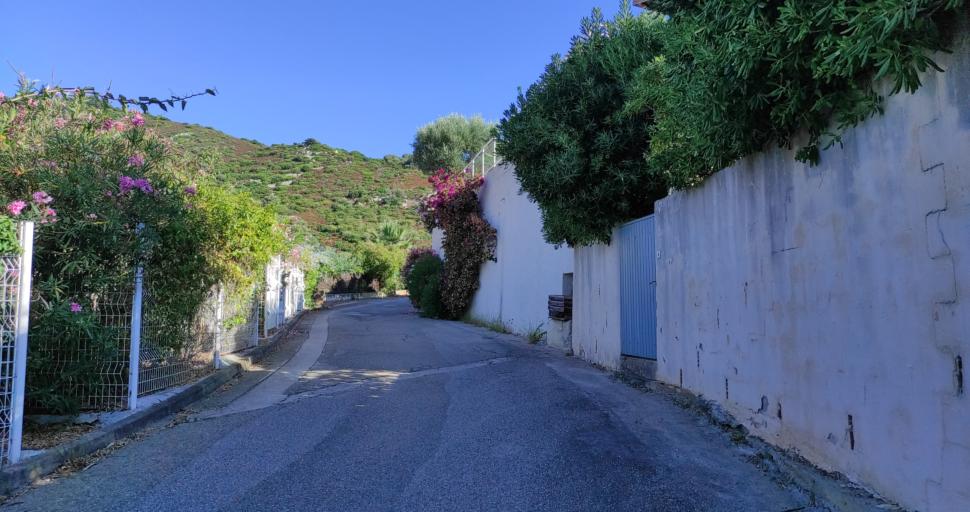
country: FR
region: Corsica
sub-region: Departement de la Corse-du-Sud
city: Alata
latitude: 41.9965
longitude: 8.6700
